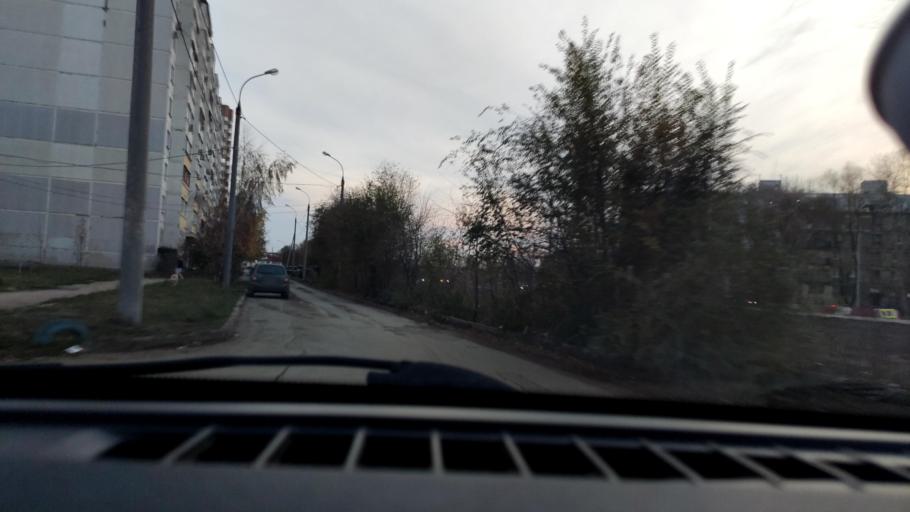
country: RU
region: Samara
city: Samara
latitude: 53.1090
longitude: 50.0818
